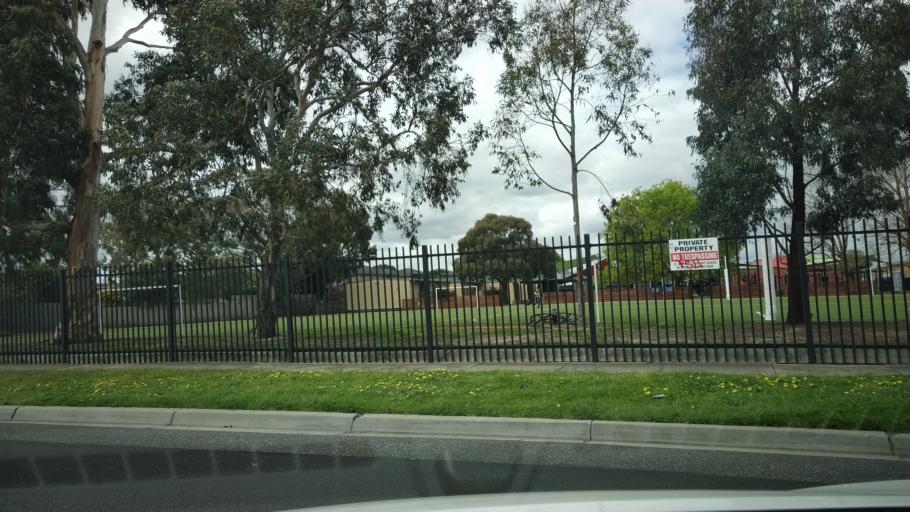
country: AU
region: Victoria
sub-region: Greater Dandenong
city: Noble Park
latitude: -37.9715
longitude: 145.1702
